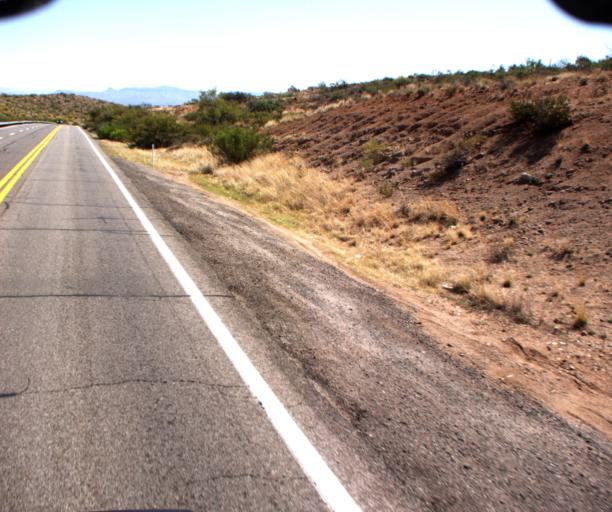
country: US
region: Arizona
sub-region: Pinal County
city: Oracle
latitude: 32.6549
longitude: -110.7017
